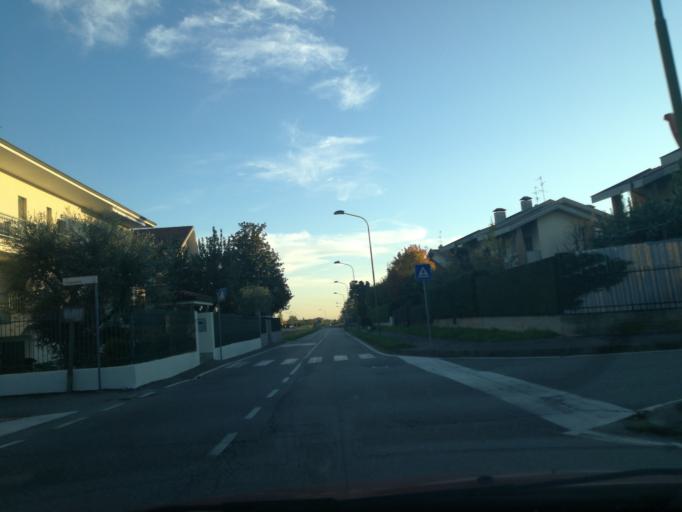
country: IT
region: Lombardy
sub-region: Provincia di Monza e Brianza
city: Burago di Molgora
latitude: 45.6090
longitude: 9.3807
